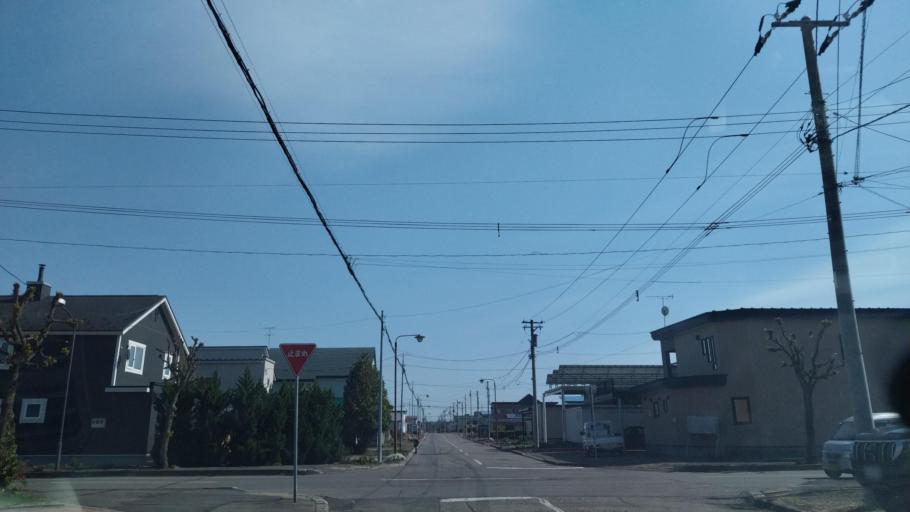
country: JP
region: Hokkaido
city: Obihiro
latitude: 42.9189
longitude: 143.0549
